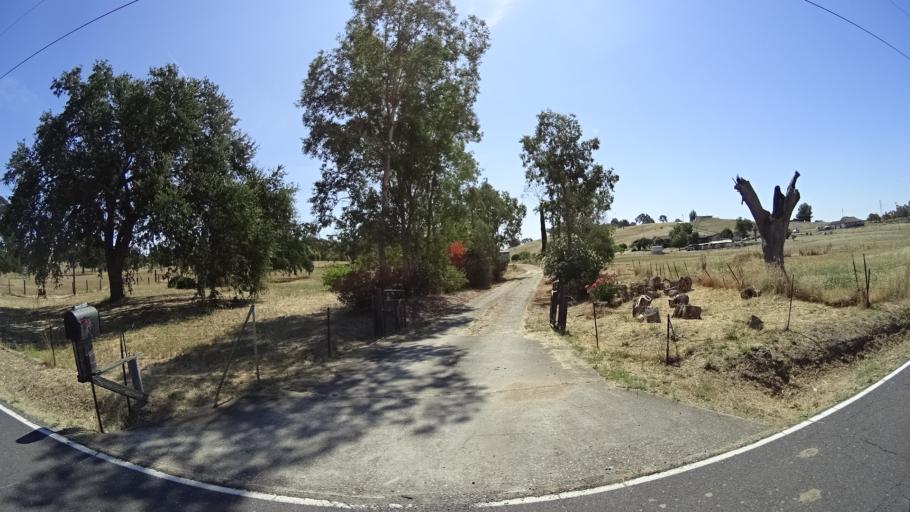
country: US
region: California
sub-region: Calaveras County
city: Rancho Calaveras
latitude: 38.0891
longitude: -120.9264
